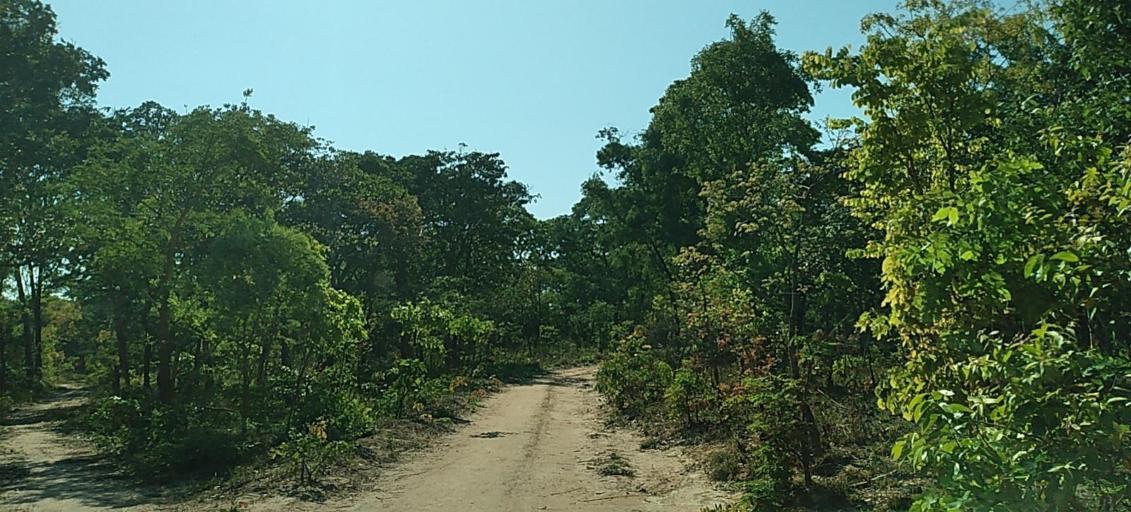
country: ZM
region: Central
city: Mkushi
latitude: -13.4713
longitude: 28.9790
